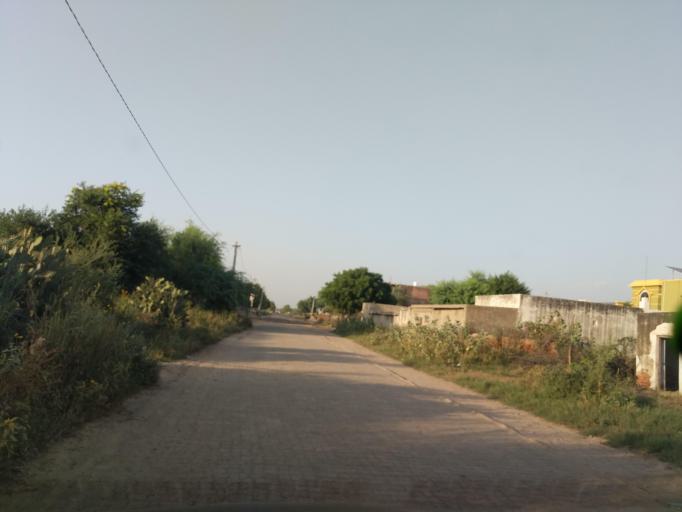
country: IN
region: Rajasthan
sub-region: Churu
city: Rajgarh
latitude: 28.5636
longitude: 75.3663
